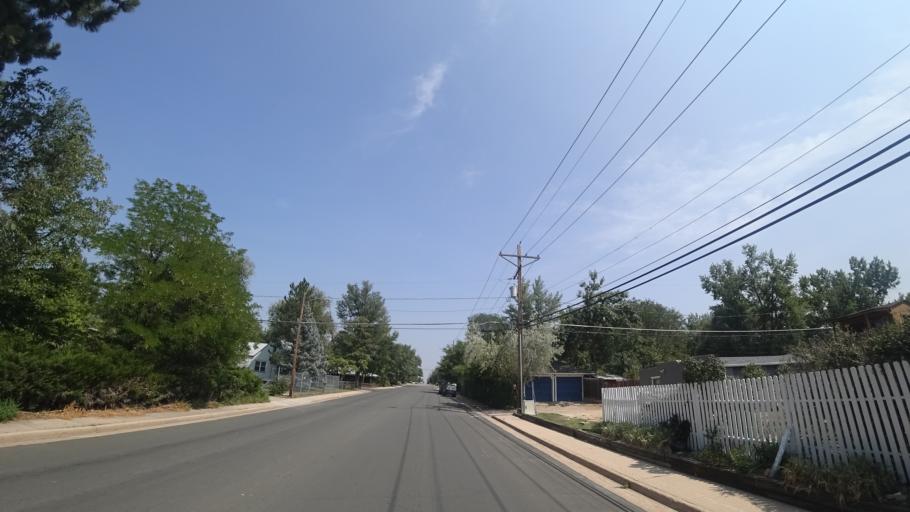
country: US
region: Colorado
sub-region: Arapahoe County
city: Englewood
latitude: 39.6386
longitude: -104.9970
